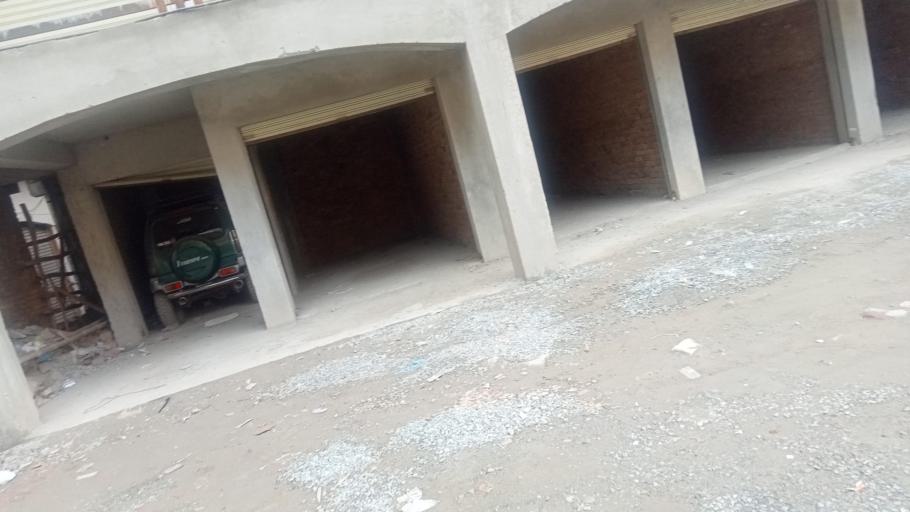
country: PK
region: Khyber Pakhtunkhwa
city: Mingora
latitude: 34.7768
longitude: 72.3572
